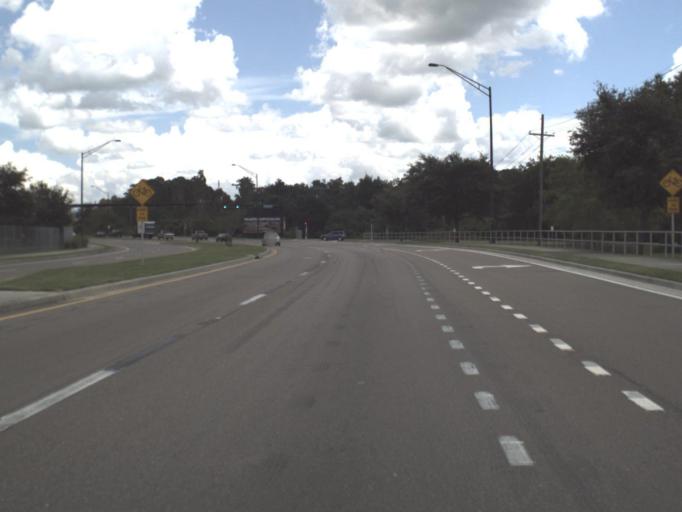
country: US
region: Florida
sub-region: Polk County
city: Bartow
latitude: 27.9007
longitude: -81.8222
